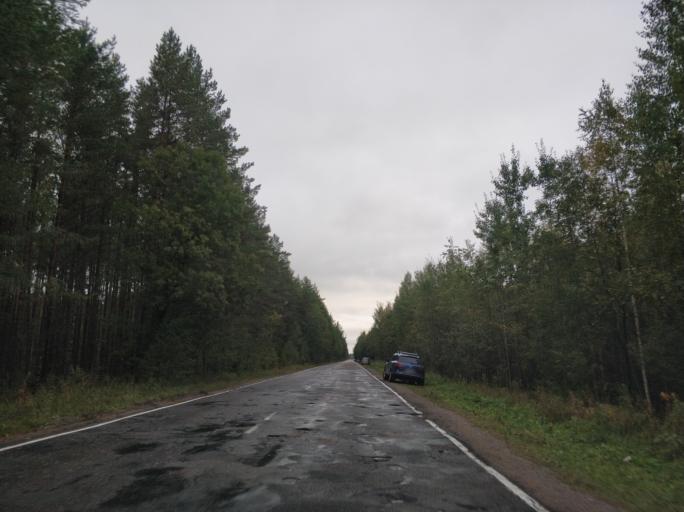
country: RU
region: Leningrad
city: Borisova Griva
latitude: 60.1706
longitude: 30.9201
